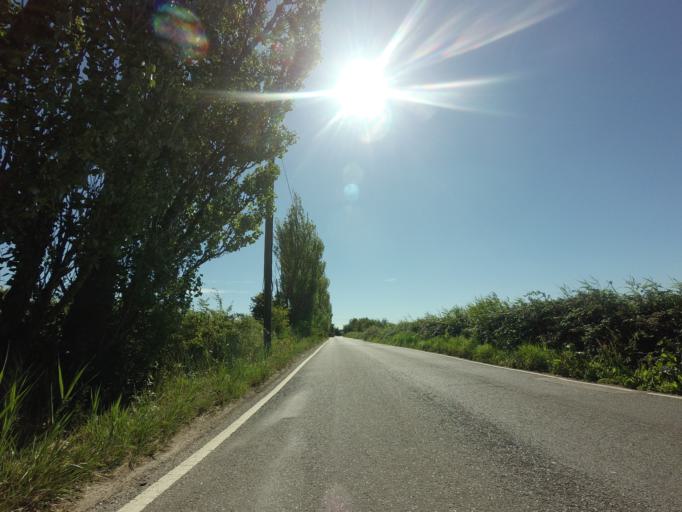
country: GB
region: England
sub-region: Kent
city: Ash
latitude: 51.3128
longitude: 1.2177
